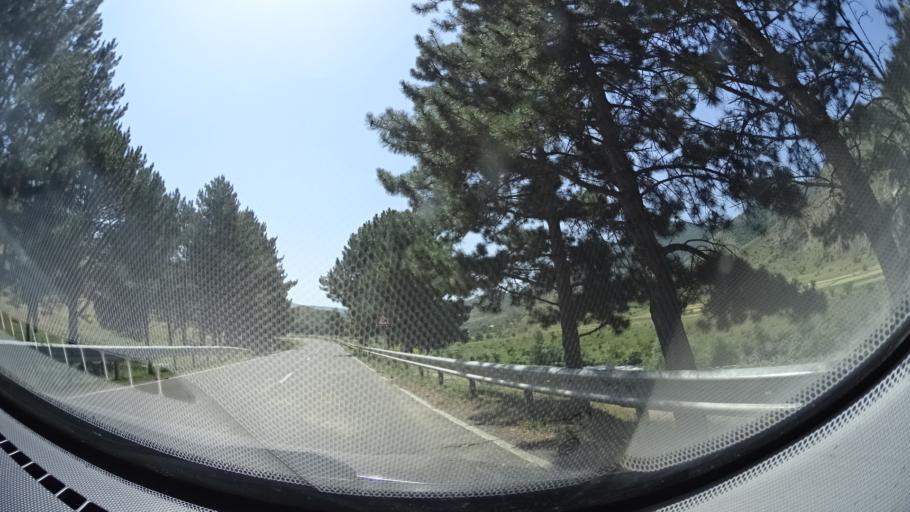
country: GE
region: Samtskhe-Javakheti
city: Aspindza
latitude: 41.4461
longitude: 43.3089
